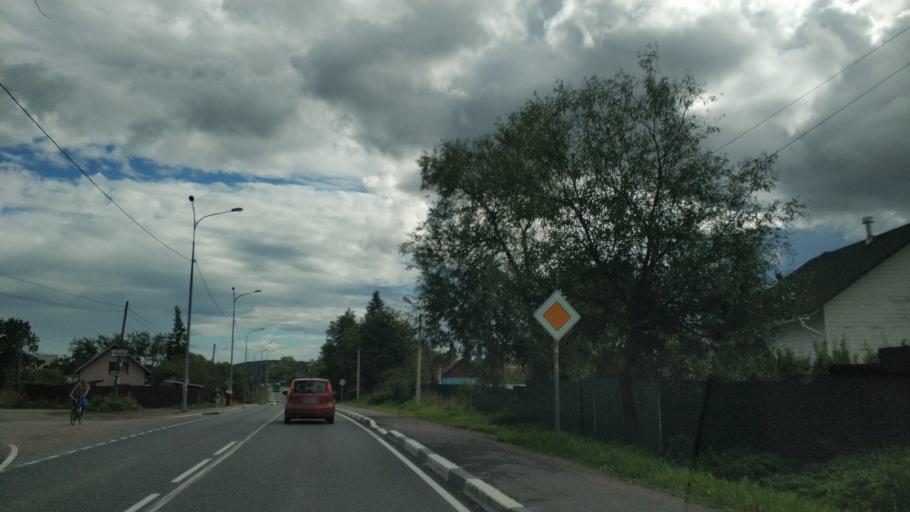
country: RU
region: Republic of Karelia
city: Khelyulya
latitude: 61.7504
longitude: 30.6623
